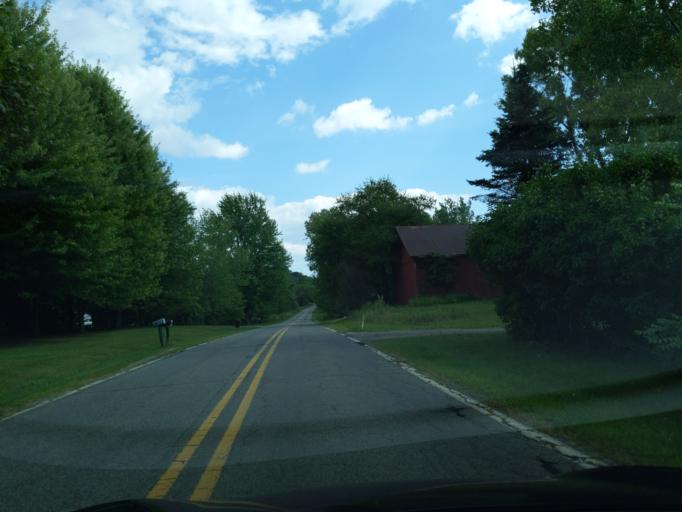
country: US
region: Michigan
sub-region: Jackson County
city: Spring Arbor
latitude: 42.3237
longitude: -84.5323
